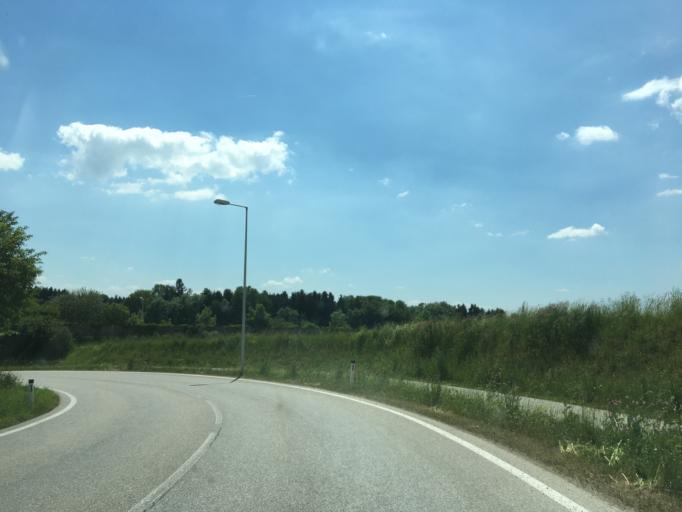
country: AT
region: Upper Austria
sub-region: Politischer Bezirk Urfahr-Umgebung
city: Engerwitzdorf
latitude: 48.3479
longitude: 14.5407
